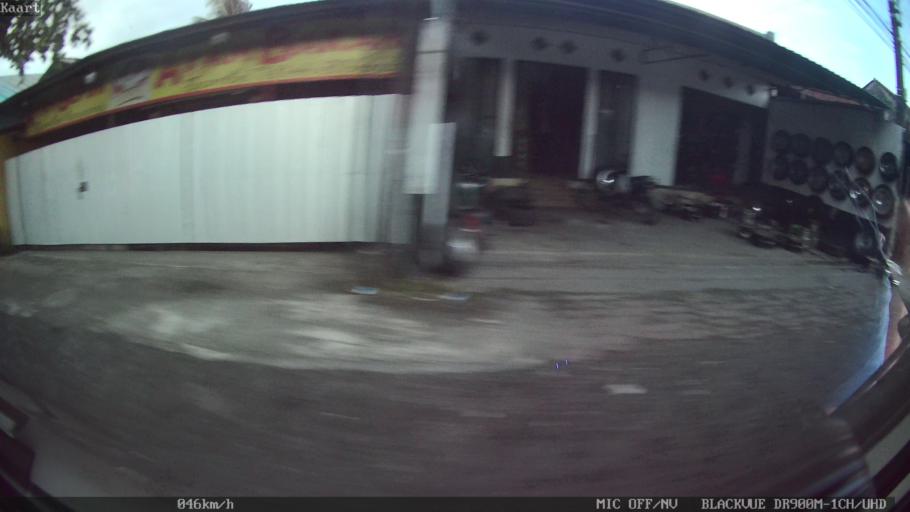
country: ID
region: Bali
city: Banjar Parekan
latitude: -8.5704
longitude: 115.2193
